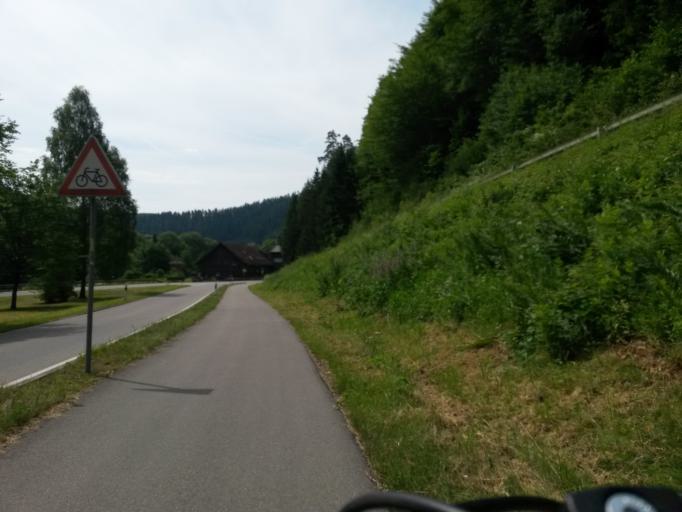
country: DE
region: Baden-Wuerttemberg
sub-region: Karlsruhe Region
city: Bad Teinach-Zavelstein
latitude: 48.6819
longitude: 8.7253
